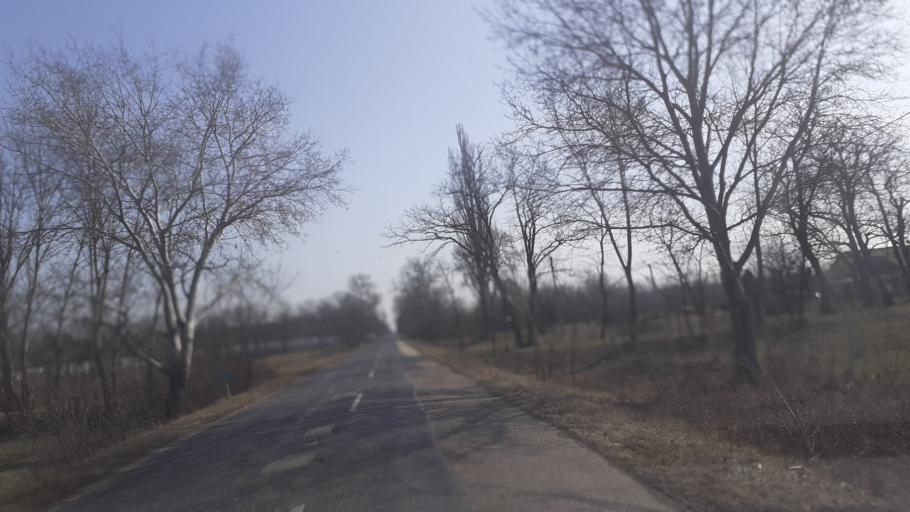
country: HU
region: Pest
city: Taborfalva
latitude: 47.0495
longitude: 19.4234
